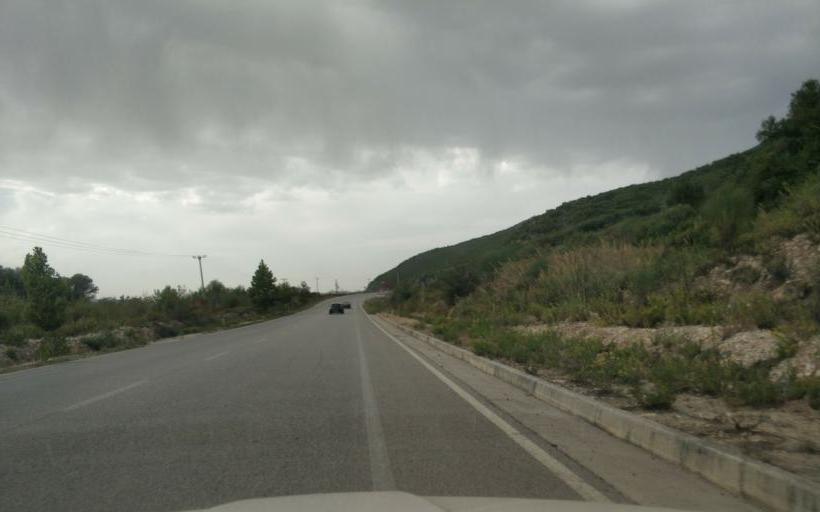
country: AL
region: Fier
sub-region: Rrethi i Mallakastres
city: Hekal
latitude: 40.5252
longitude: 19.7362
